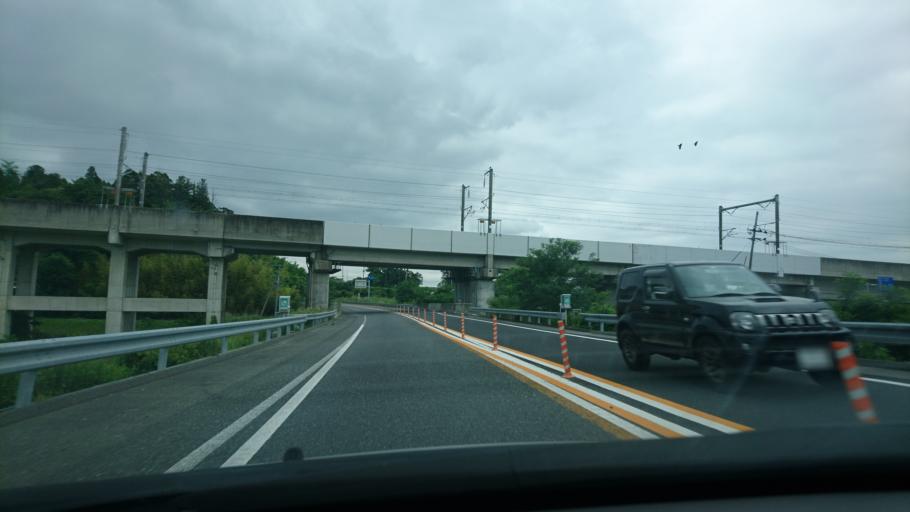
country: JP
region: Miyagi
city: Kogota
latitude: 38.7290
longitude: 141.0596
